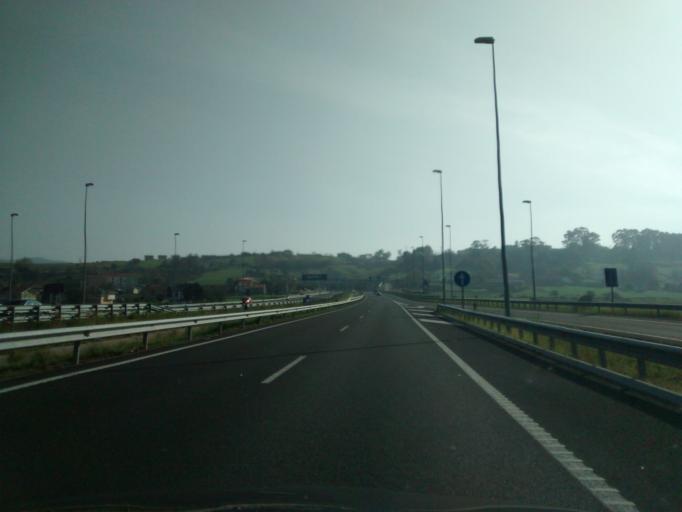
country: ES
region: Cantabria
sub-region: Provincia de Cantabria
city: Camargo
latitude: 43.4034
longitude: -3.8701
